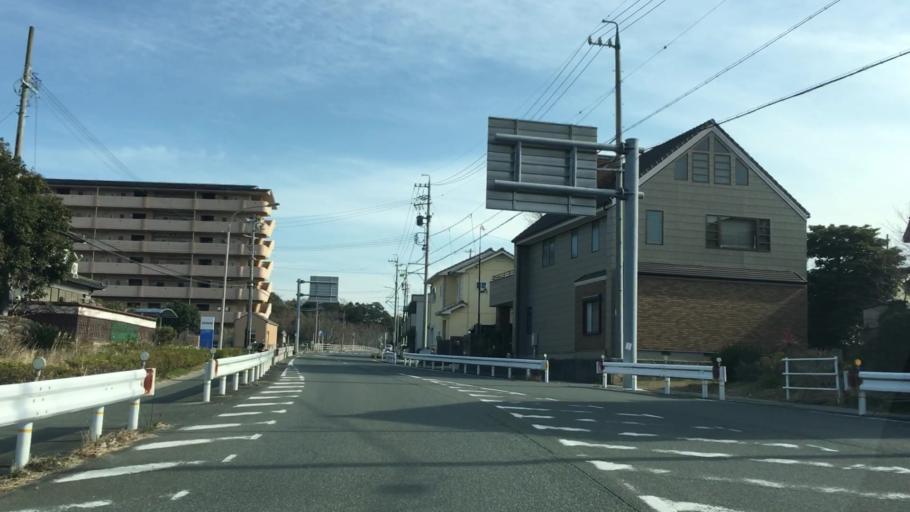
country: JP
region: Aichi
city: Tahara
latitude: 34.6624
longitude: 137.2775
